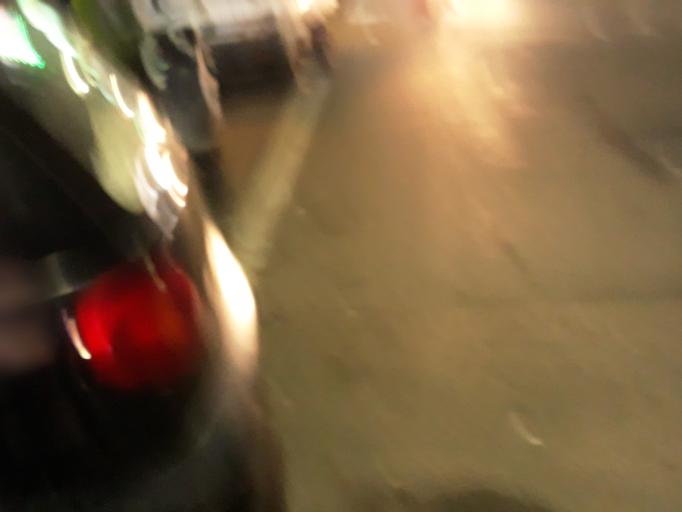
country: TW
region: Taiwan
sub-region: Hsinchu
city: Hsinchu
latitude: 24.8161
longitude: 120.9769
